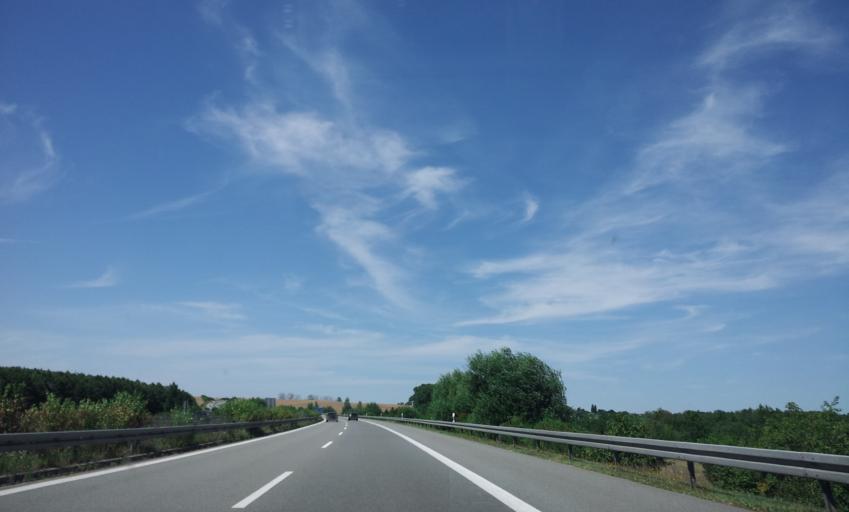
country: DE
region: Mecklenburg-Vorpommern
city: Neuenkirchen
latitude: 53.5861
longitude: 13.4132
